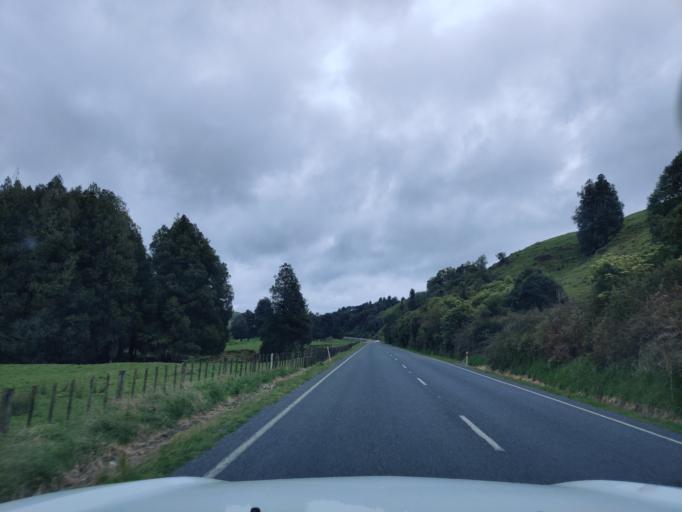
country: NZ
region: Waikato
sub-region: Otorohanga District
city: Otorohanga
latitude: -38.5475
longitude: 175.1857
